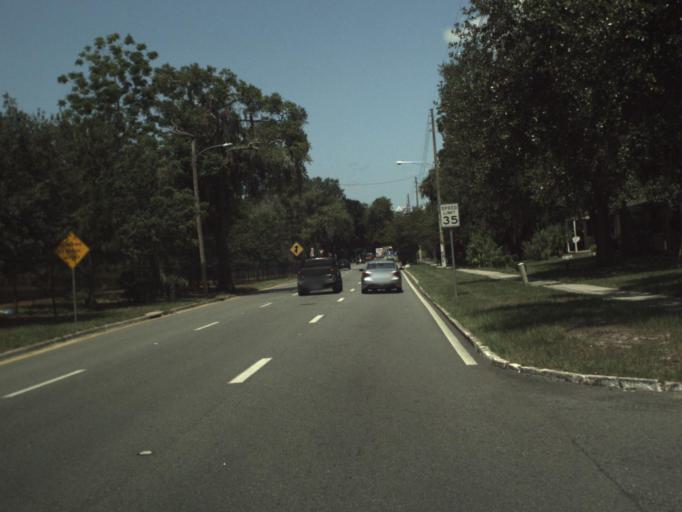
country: US
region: Florida
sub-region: Orange County
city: Orlando
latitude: 28.5386
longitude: -81.3606
